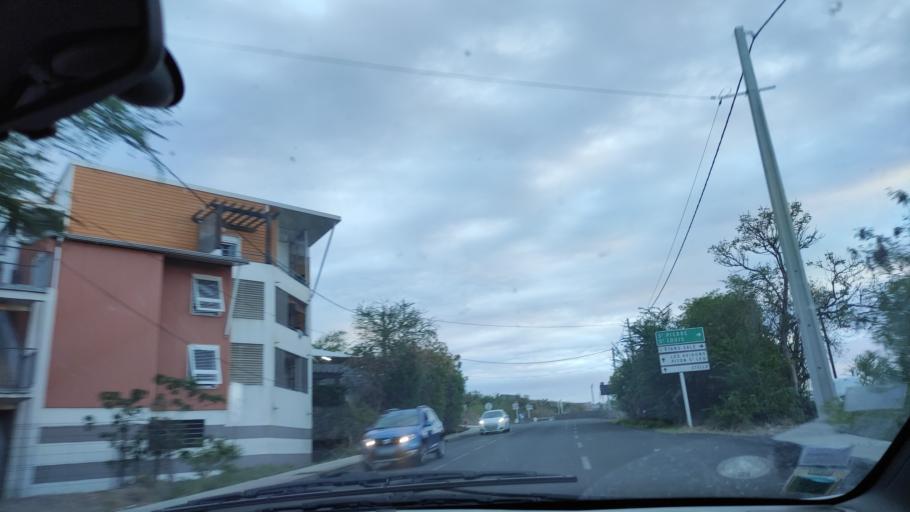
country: RE
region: Reunion
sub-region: Reunion
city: Saint-Leu
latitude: -21.1984
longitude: 55.2933
